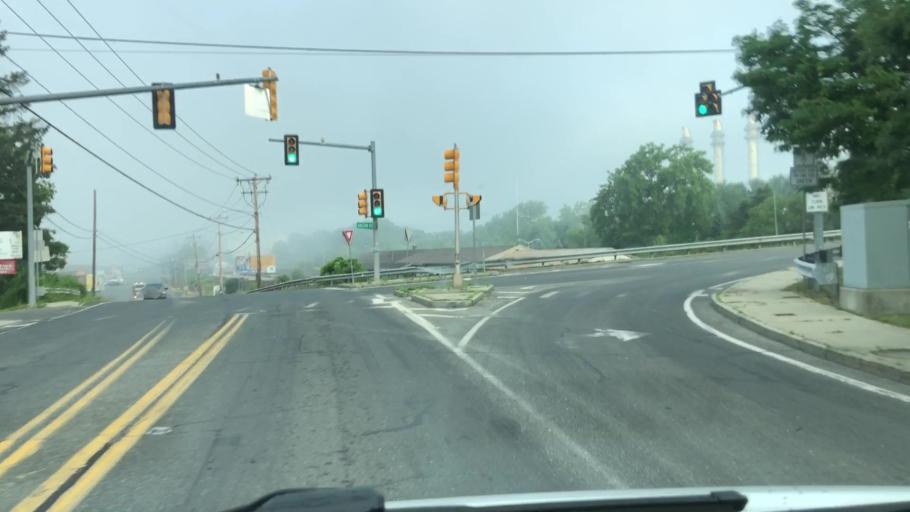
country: US
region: Massachusetts
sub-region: Berkshire County
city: Pittsfield
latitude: 42.4547
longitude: -73.2129
